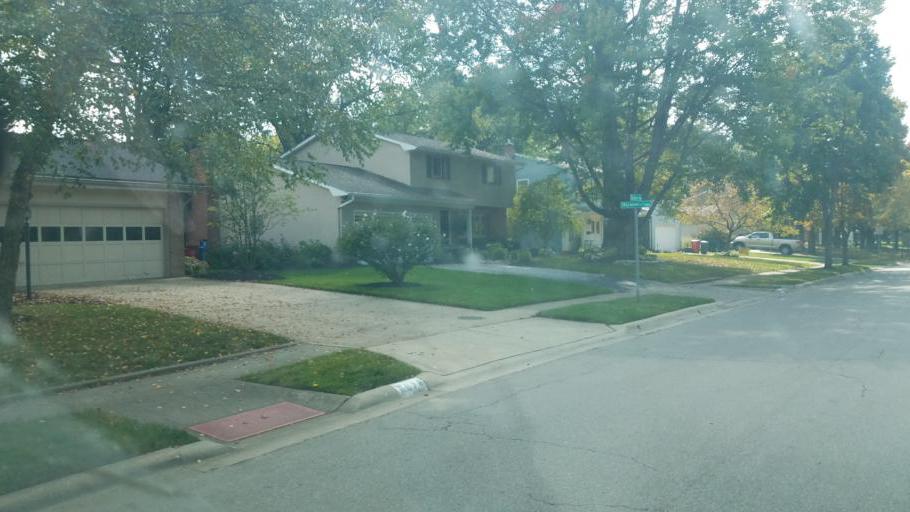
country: US
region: Ohio
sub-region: Franklin County
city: Worthington
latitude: 40.1053
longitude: -83.0281
